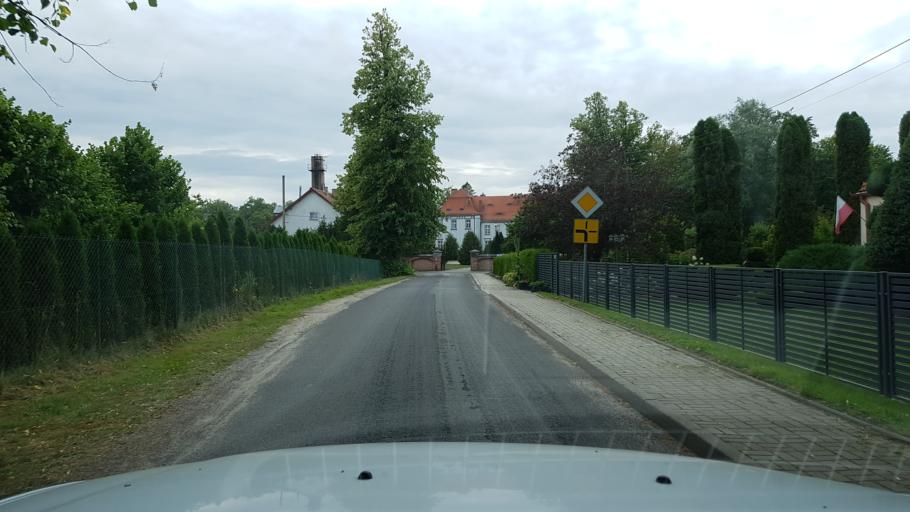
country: PL
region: West Pomeranian Voivodeship
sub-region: Powiat bialogardzki
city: Bialogard
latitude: 54.0944
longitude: 15.9738
